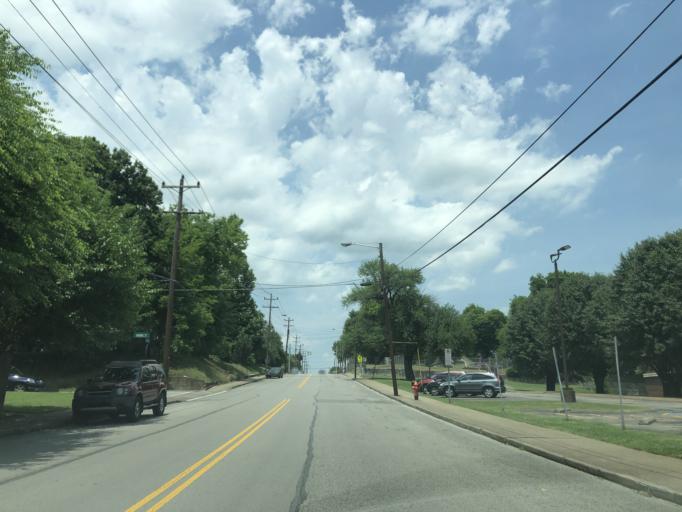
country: US
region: Tennessee
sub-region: Davidson County
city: Nashville
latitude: 36.1799
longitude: -86.7551
